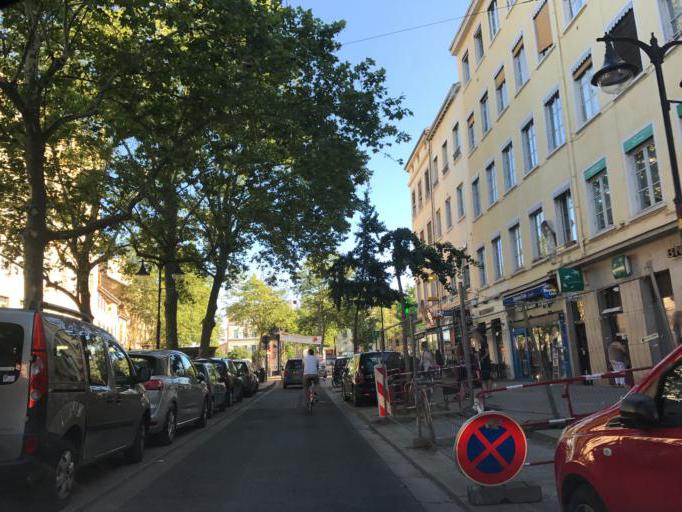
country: FR
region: Rhone-Alpes
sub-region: Departement du Rhone
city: Caluire-et-Cuire
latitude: 45.7758
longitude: 4.8323
